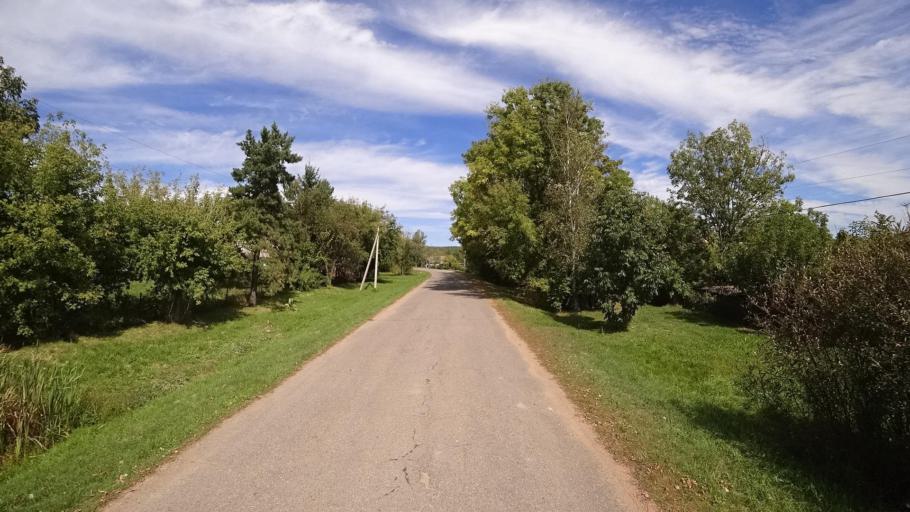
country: RU
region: Primorskiy
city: Yakovlevka
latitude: 44.6454
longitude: 133.5959
